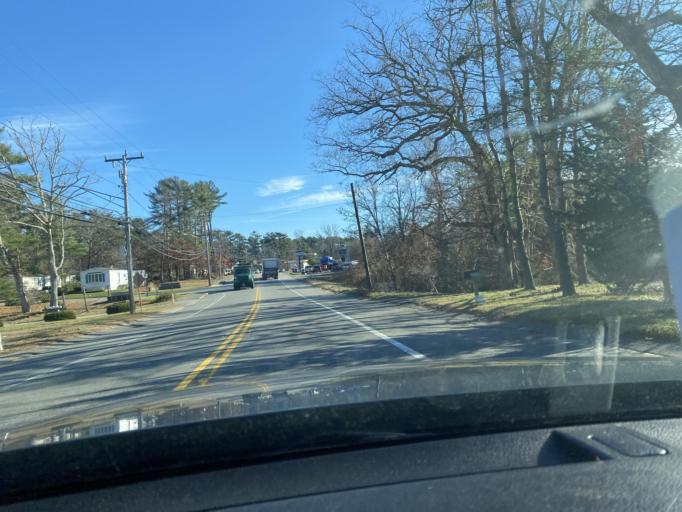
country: US
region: Massachusetts
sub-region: Plymouth County
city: West Wareham
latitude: 41.7910
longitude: -70.7542
